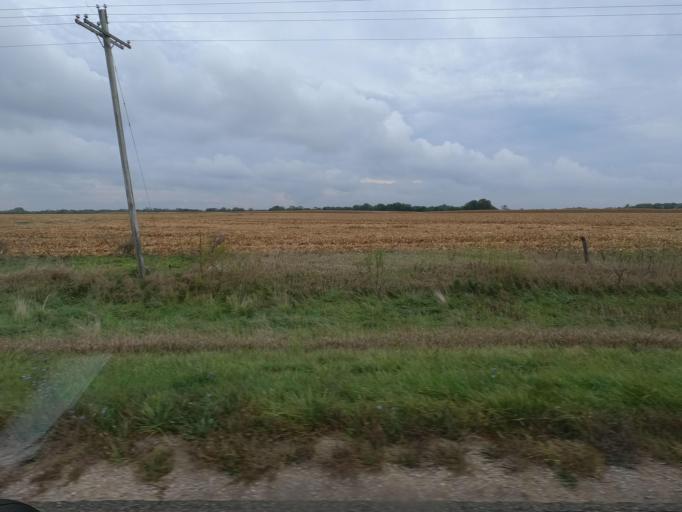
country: US
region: Iowa
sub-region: Van Buren County
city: Keosauqua
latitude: 40.8101
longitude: -91.9165
